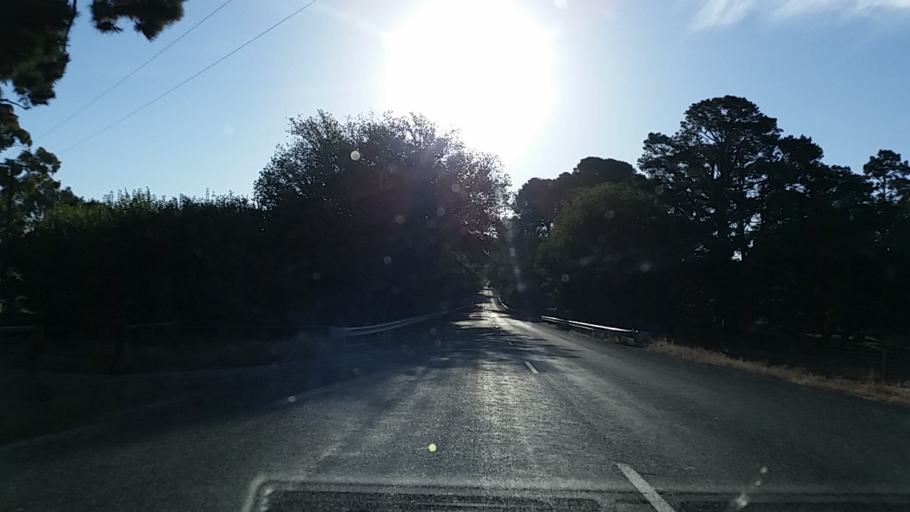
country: AU
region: South Australia
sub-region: Adelaide Hills
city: Birdwood
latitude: -34.7747
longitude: 139.0930
